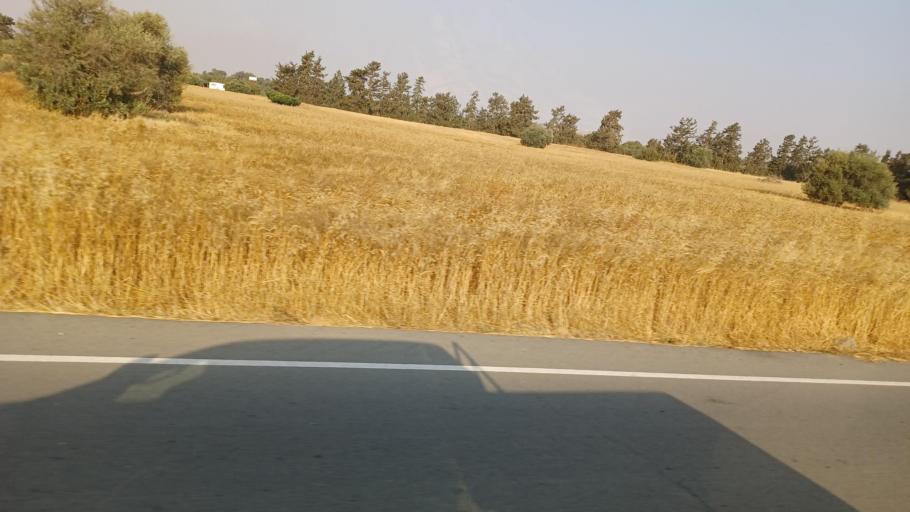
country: CY
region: Larnaka
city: Tersefanou
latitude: 34.8274
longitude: 33.5119
